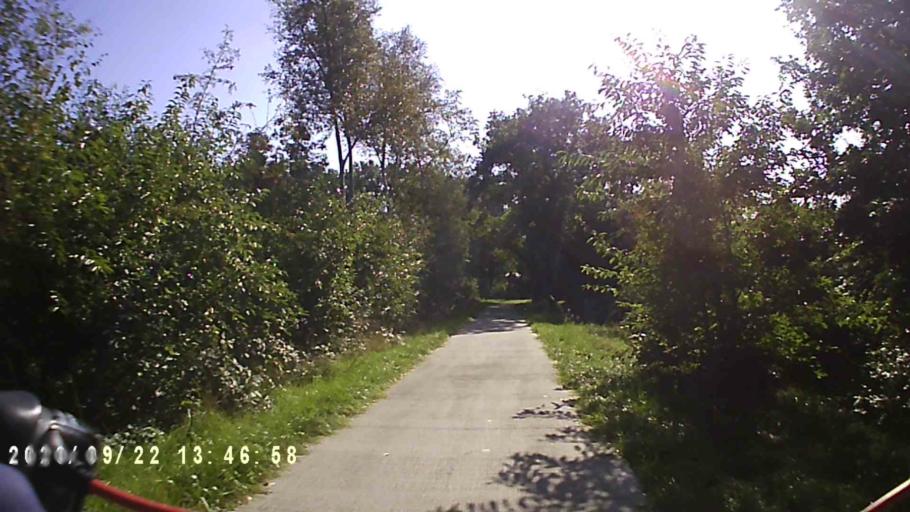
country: NL
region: Groningen
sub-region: Gemeente Leek
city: Leek
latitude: 53.1416
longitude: 6.4098
